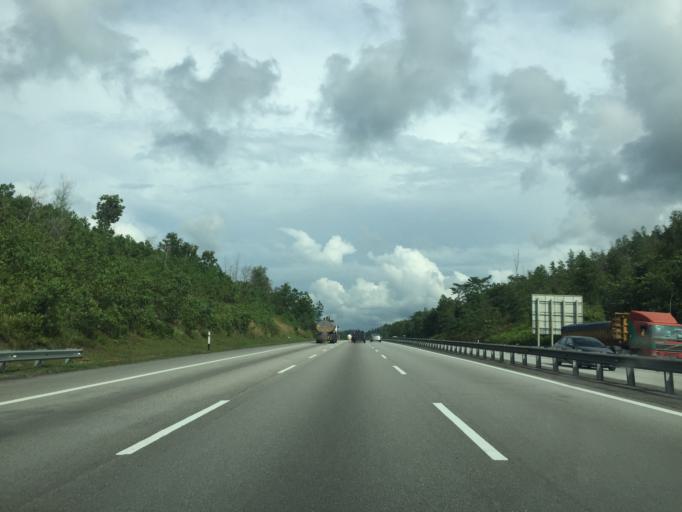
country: MY
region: Selangor
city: Serendah
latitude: 3.5188
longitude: 101.5263
